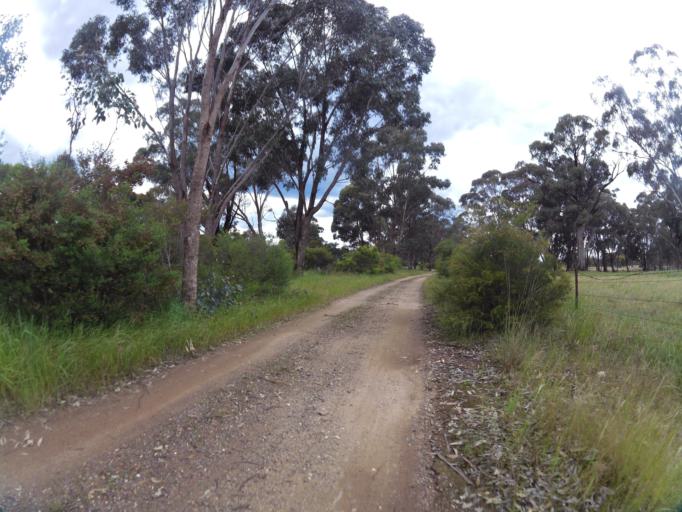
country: AU
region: Victoria
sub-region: Mount Alexander
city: Castlemaine
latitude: -37.0256
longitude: 144.1594
